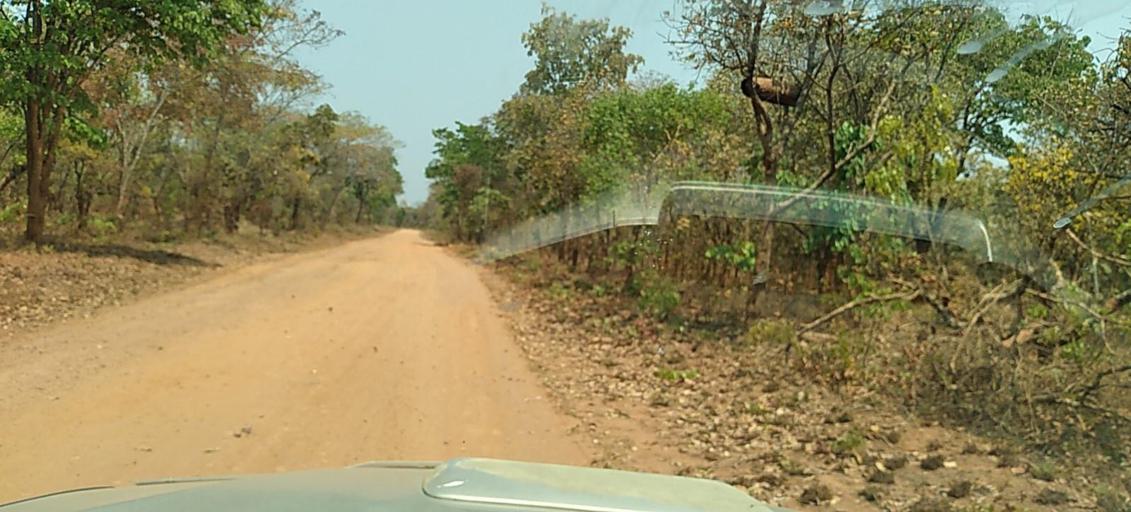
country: ZM
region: North-Western
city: Kasempa
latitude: -13.6885
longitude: 26.3215
